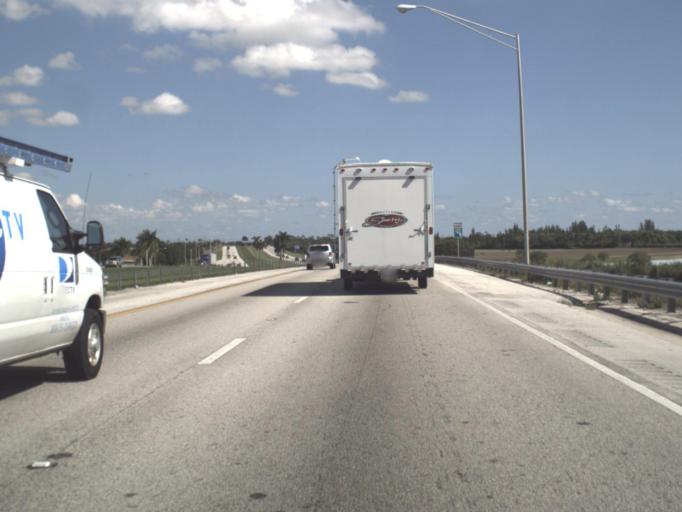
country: US
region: Florida
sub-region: Miami-Dade County
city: Naranja
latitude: 25.5110
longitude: -80.4116
